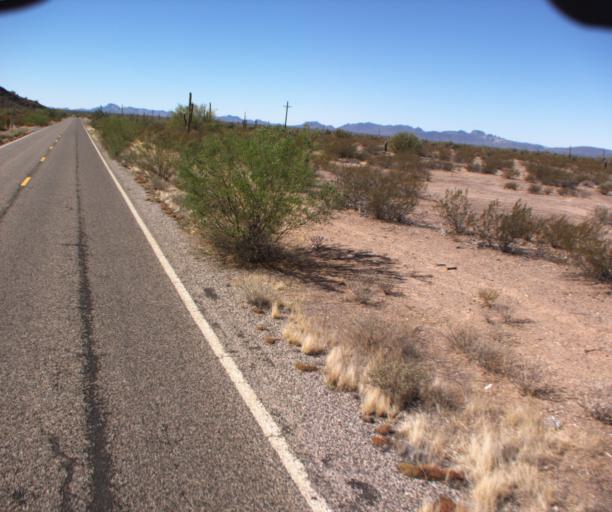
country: US
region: Arizona
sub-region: Pima County
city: Ajo
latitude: 32.2333
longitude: -112.7525
